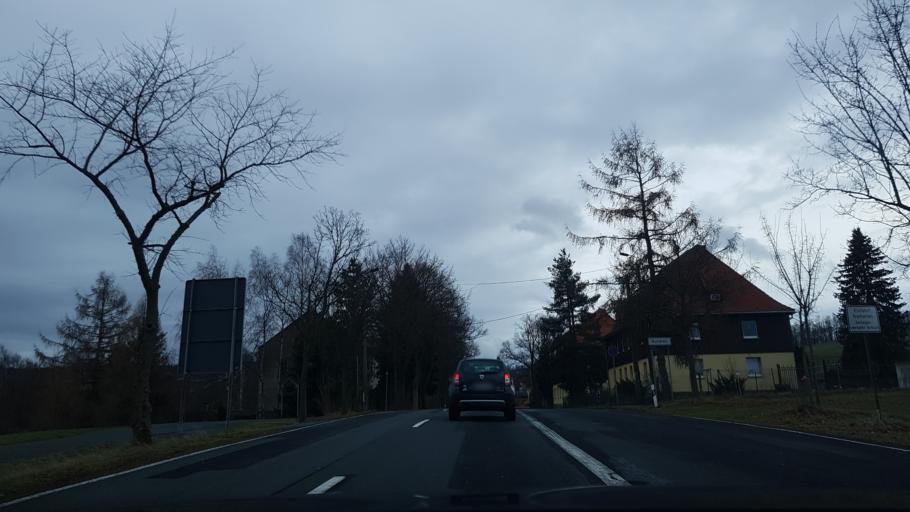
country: CZ
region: Ustecky
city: Libouchec
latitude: 50.8169
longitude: 13.9813
